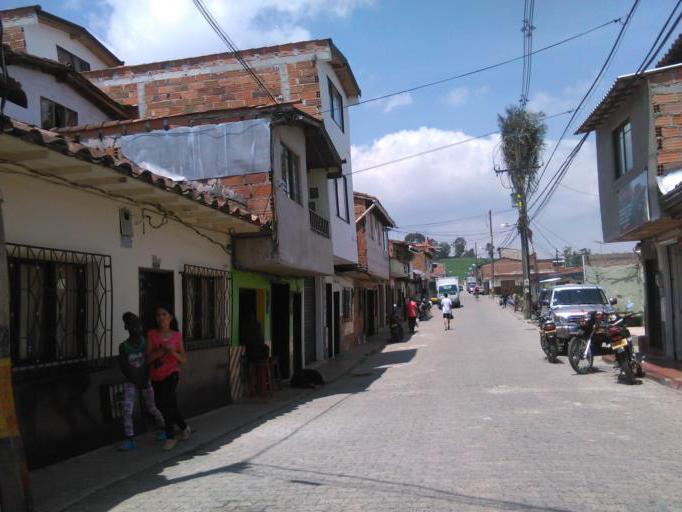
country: CO
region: Antioquia
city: La Union
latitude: 5.9744
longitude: -75.3630
